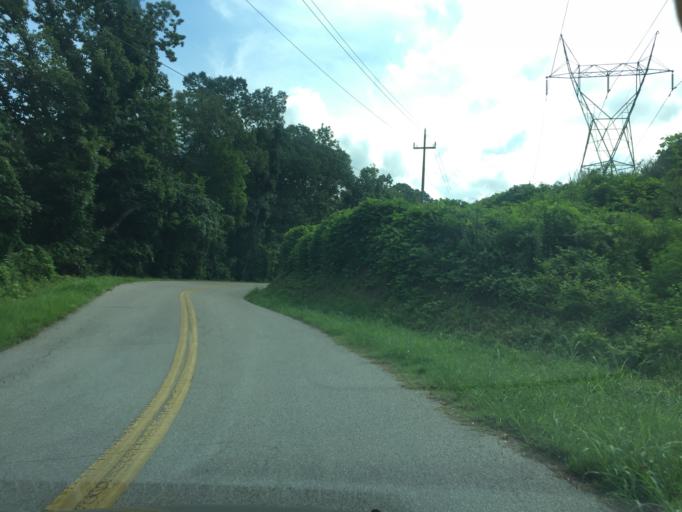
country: US
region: Tennessee
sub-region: Hamilton County
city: East Chattanooga
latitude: 35.0949
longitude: -85.2090
